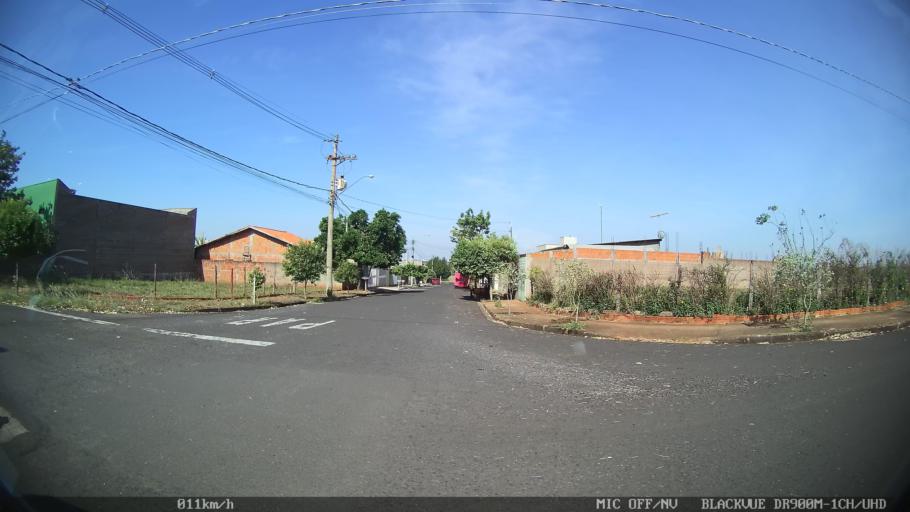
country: BR
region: Sao Paulo
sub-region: Sao Jose Do Rio Preto
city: Sao Jose do Rio Preto
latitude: -20.7933
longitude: -49.4422
